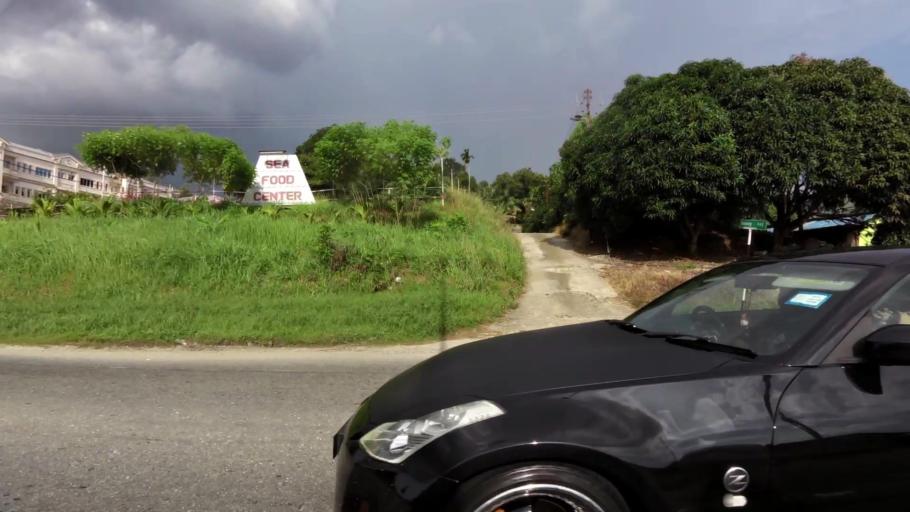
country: BN
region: Brunei and Muara
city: Bandar Seri Begawan
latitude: 4.9606
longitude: 114.9745
